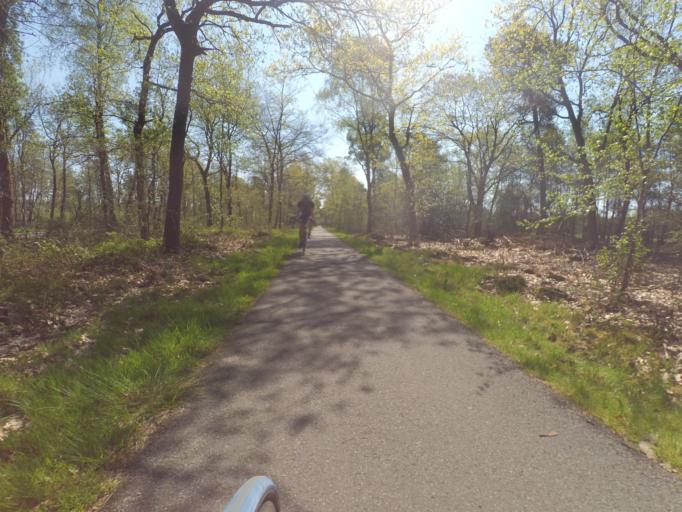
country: NL
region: Gelderland
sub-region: Gemeente Apeldoorn
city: Uddel
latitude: 52.2557
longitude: 5.7959
